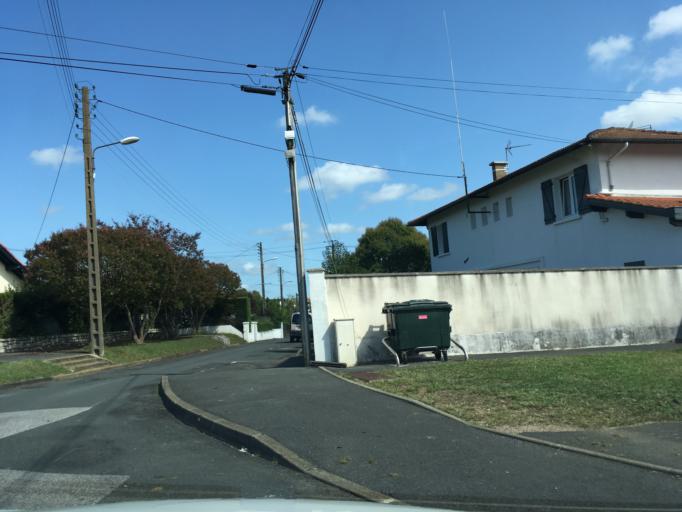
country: FR
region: Aquitaine
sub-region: Departement des Pyrenees-Atlantiques
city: Bayonne
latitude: 43.4867
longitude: -1.4944
